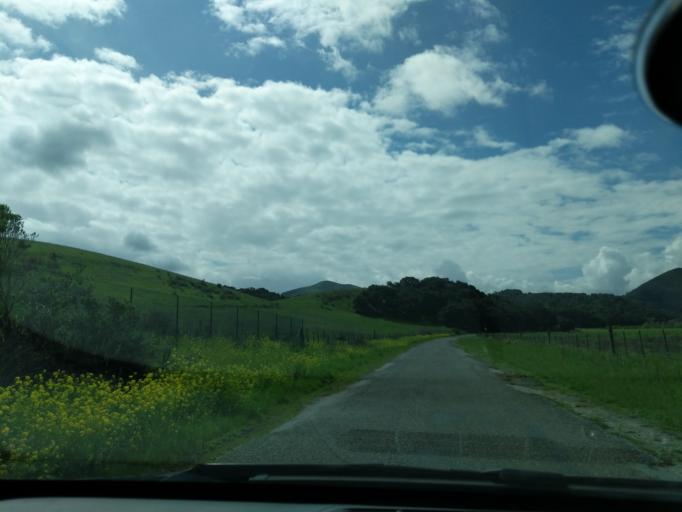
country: US
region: California
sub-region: San Benito County
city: San Juan Bautista
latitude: 36.7880
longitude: -121.5805
